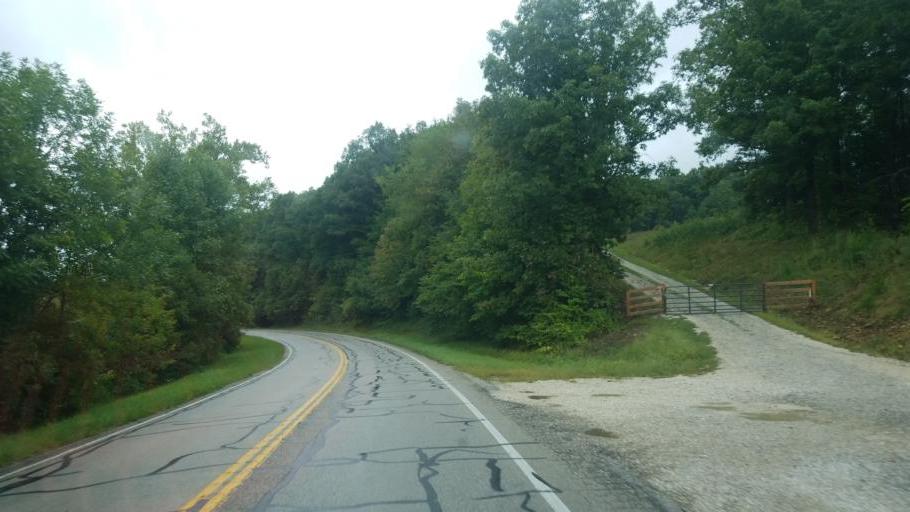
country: US
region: Kentucky
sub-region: Rowan County
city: Morehead
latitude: 38.1503
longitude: -83.4842
